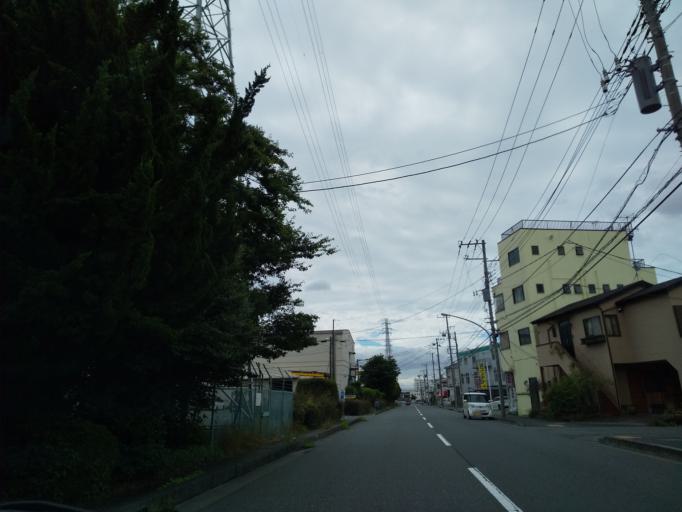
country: JP
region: Kanagawa
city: Zama
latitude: 35.5144
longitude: 139.3408
